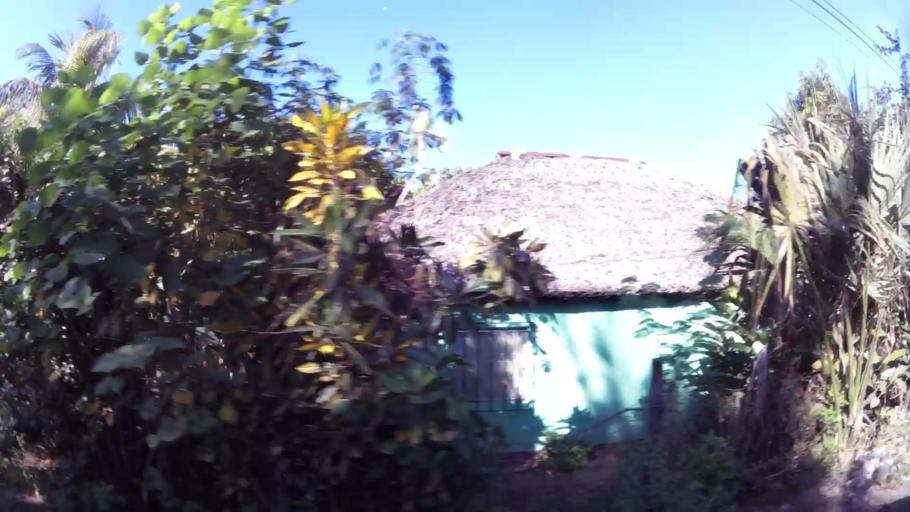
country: GT
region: Santa Rosa
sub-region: Municipio de Taxisco
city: Taxisco
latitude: 13.8961
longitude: -90.4899
